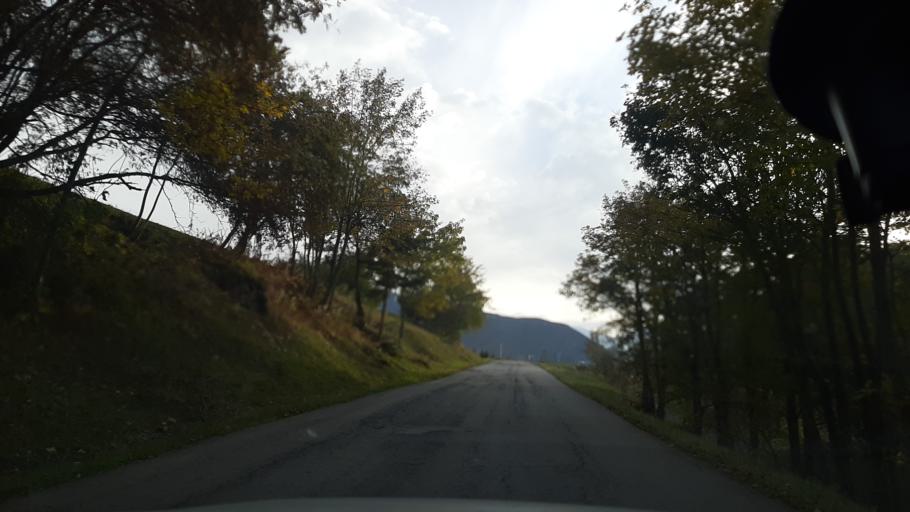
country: FR
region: Rhone-Alpes
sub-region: Departement de la Savoie
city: Villargondran
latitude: 45.2119
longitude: 6.3383
